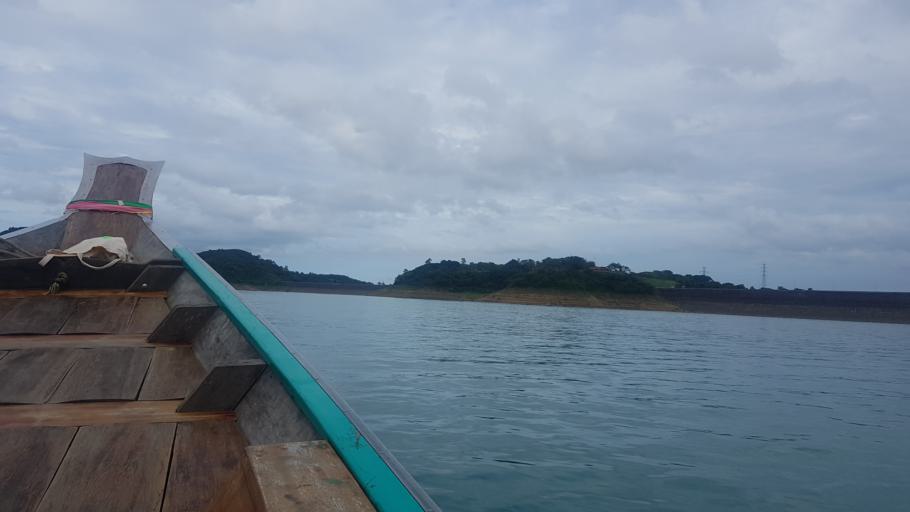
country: TH
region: Surat Thani
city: Ban Takhun
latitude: 8.9785
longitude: 98.8042
